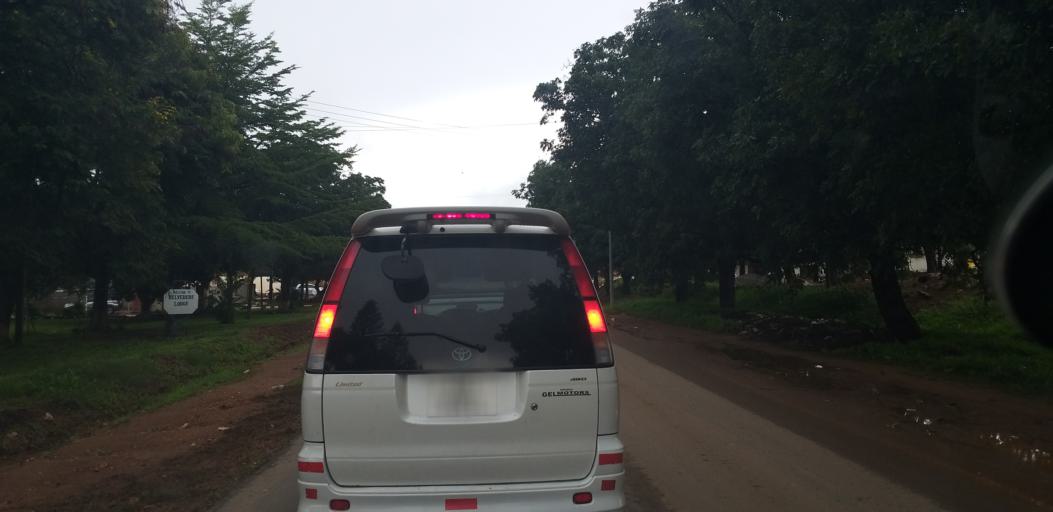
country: ZM
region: Lusaka
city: Lusaka
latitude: -15.4291
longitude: 28.3416
